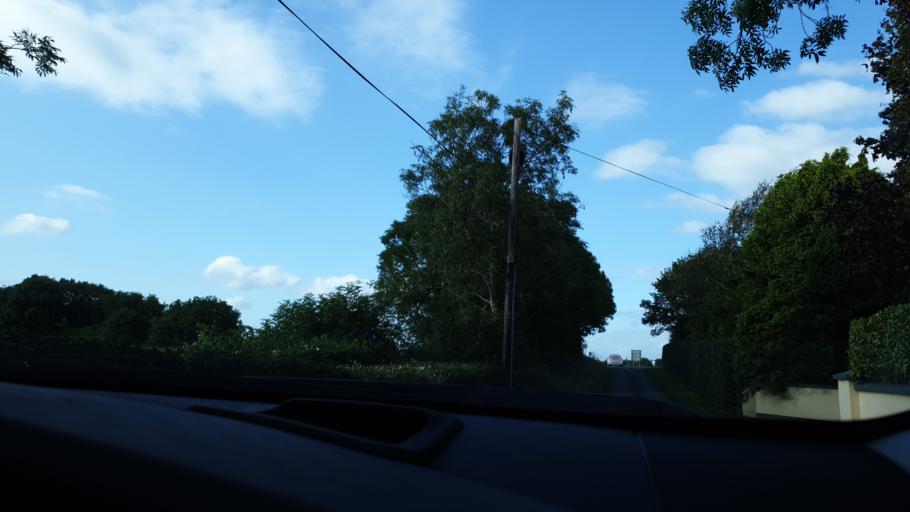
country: IE
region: Leinster
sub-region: An Mhi
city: Ashbourne
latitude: 53.4958
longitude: -6.4037
